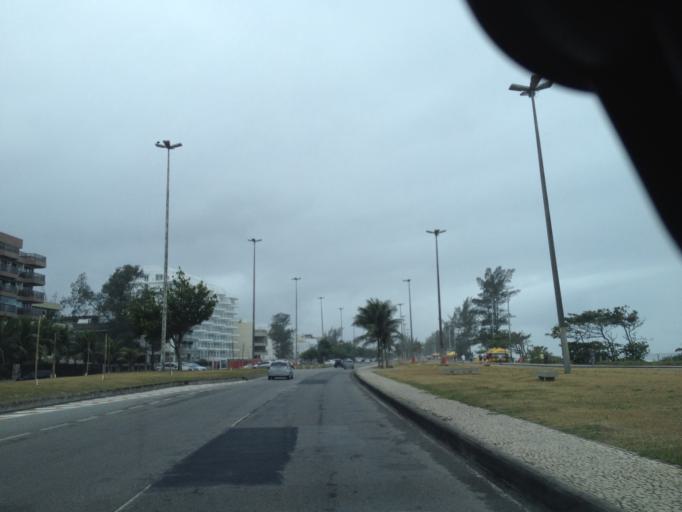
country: BR
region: Rio de Janeiro
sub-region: Nilopolis
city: Nilopolis
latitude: -23.0284
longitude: -43.4667
